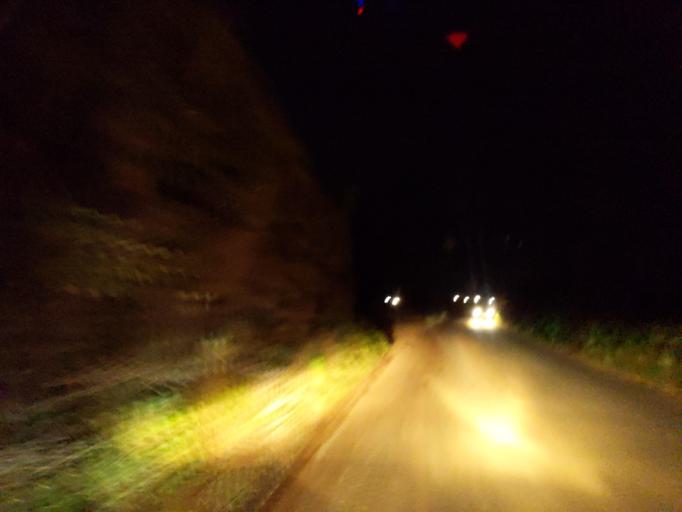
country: GB
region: England
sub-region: Cornwall
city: Torpoint
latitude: 50.3499
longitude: -4.2298
